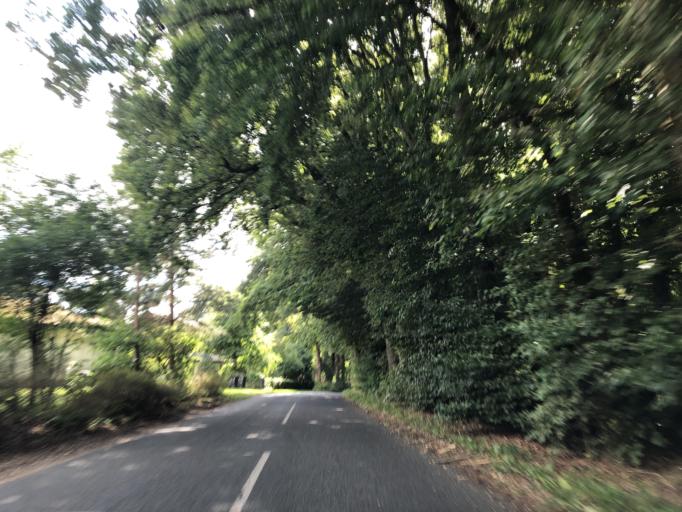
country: DK
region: North Denmark
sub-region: Vesthimmerland Kommune
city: Alestrup
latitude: 56.6060
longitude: 9.4343
